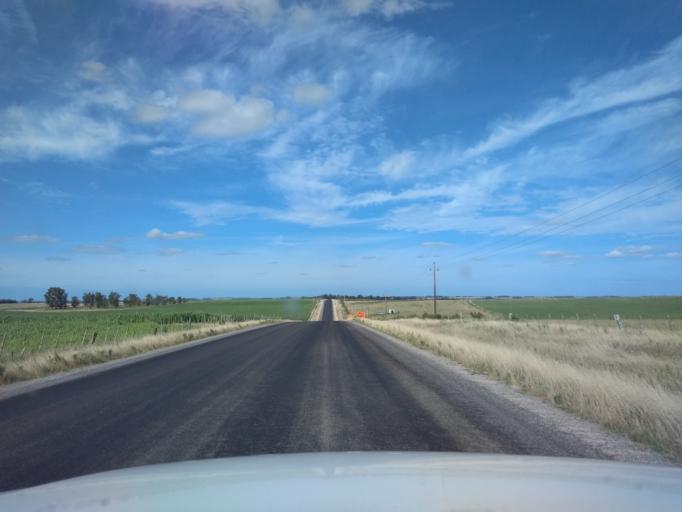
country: UY
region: Florida
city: Casupa
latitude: -34.0345
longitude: -55.8821
